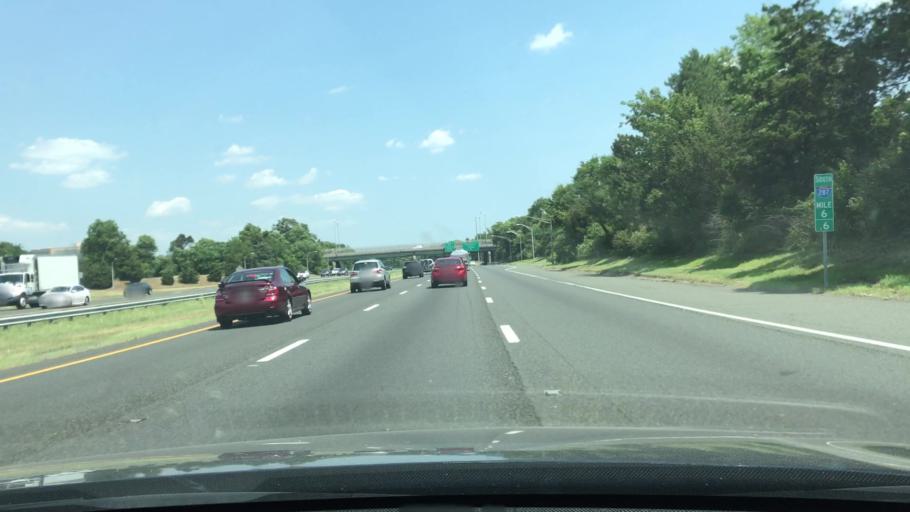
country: US
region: New Jersey
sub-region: Middlesex County
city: Society Hill
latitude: 40.5556
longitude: -74.4497
